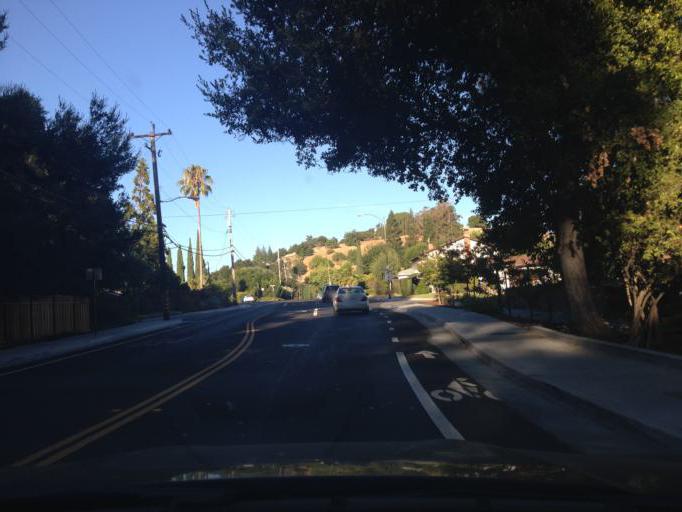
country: US
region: California
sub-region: Santa Clara County
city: Los Gatos
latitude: 37.2348
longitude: -121.9523
